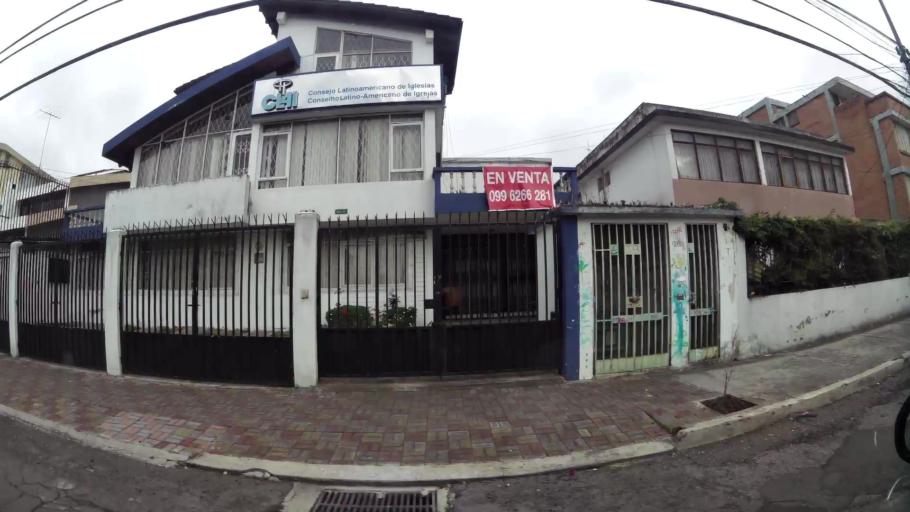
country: EC
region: Pichincha
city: Quito
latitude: -0.1878
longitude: -78.4905
